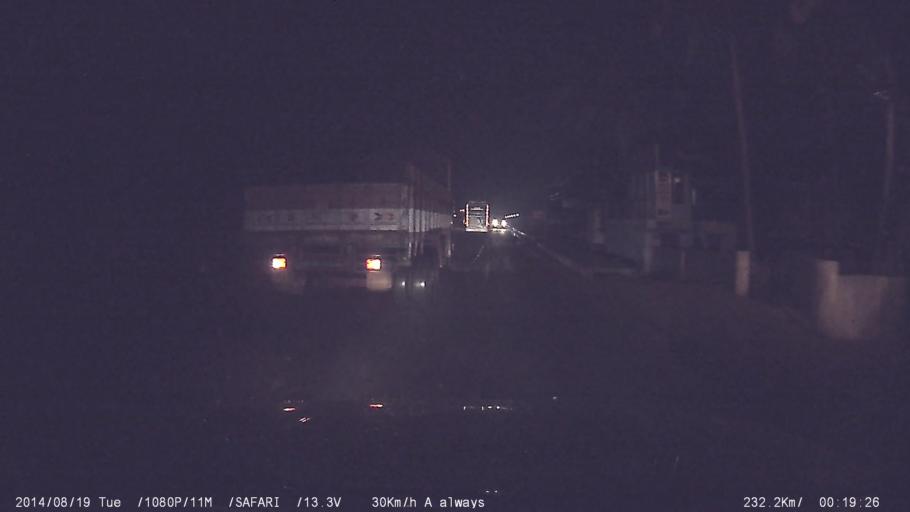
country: IN
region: Kerala
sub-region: Palakkad district
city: Palakkad
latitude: 10.7938
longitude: 76.7337
